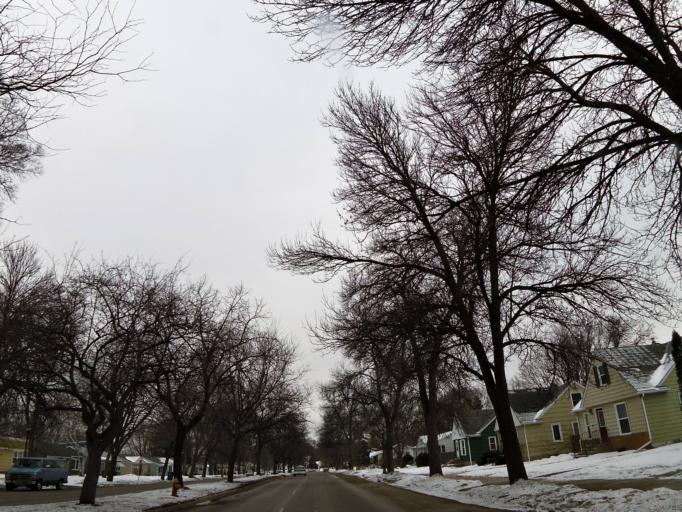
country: US
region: Minnesota
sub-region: Dakota County
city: Mendota Heights
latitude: 44.9067
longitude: -93.1804
